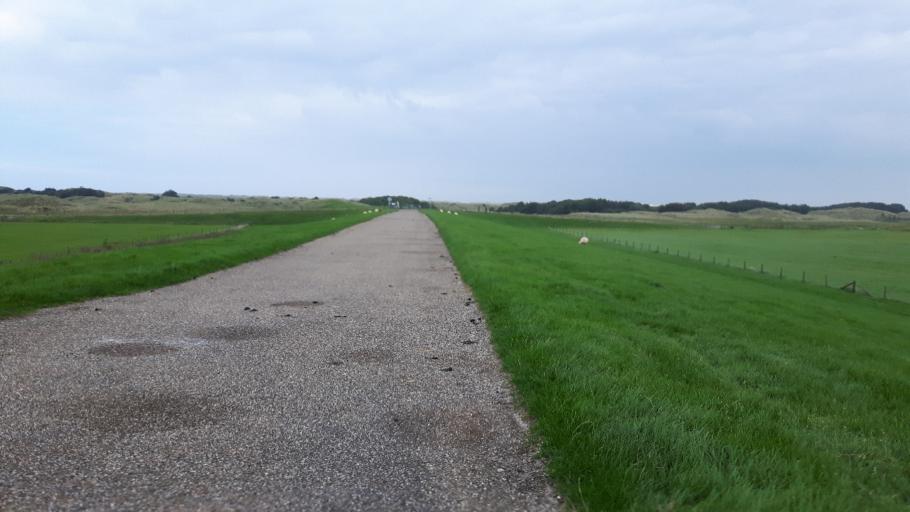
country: NL
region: Friesland
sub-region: Gemeente Ameland
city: Nes
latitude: 53.4461
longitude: 5.8492
